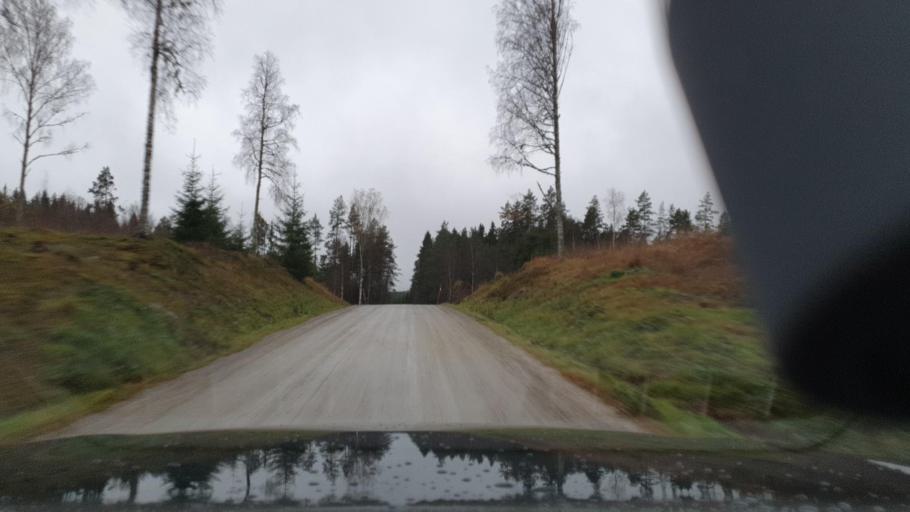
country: SE
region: Vaermland
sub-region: Arvika Kommun
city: Arvika
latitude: 59.8256
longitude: 12.7455
